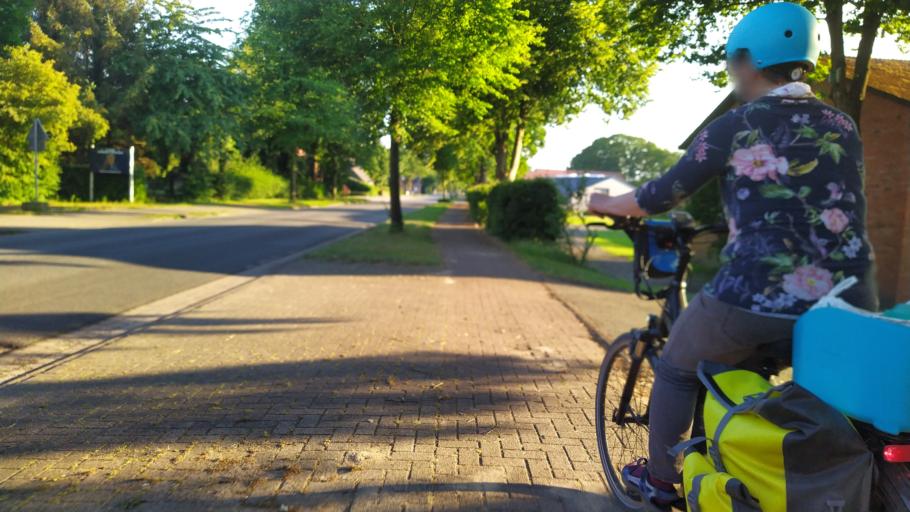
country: DE
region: Lower Saxony
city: Alfstedt
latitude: 53.5484
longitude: 9.0671
